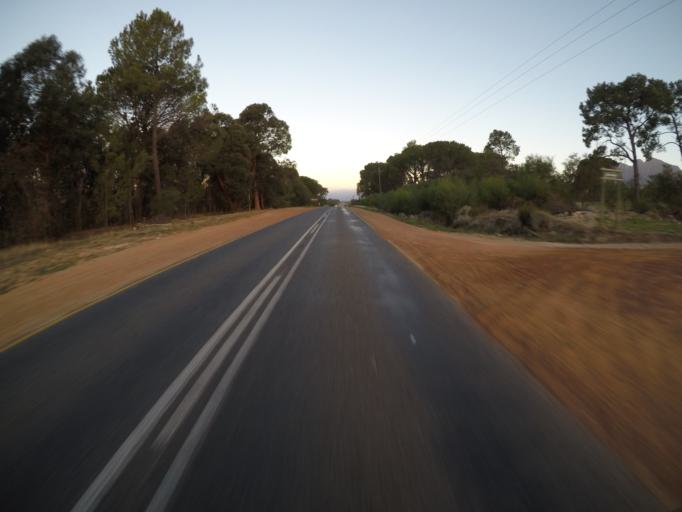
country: ZA
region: Western Cape
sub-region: Cape Winelands District Municipality
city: Paarl
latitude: -33.8125
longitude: 18.9110
